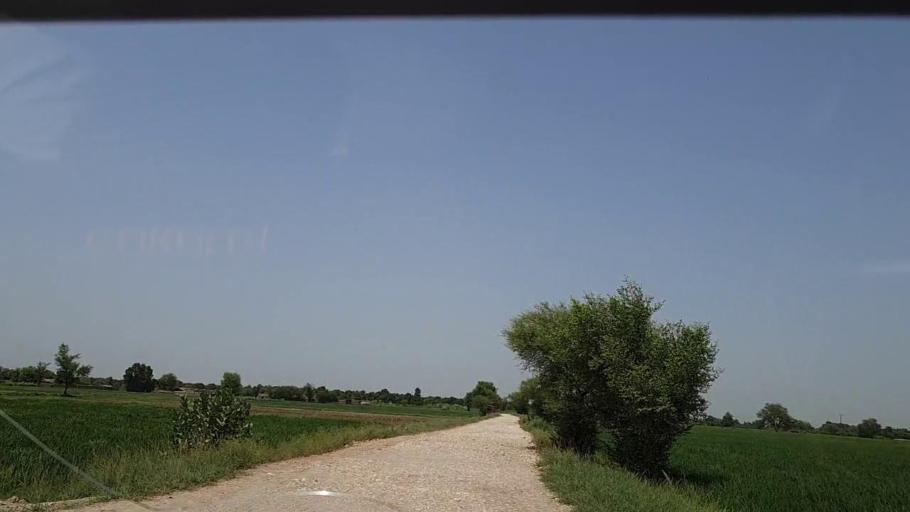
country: PK
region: Sindh
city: Tharu Shah
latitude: 26.9571
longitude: 68.0434
